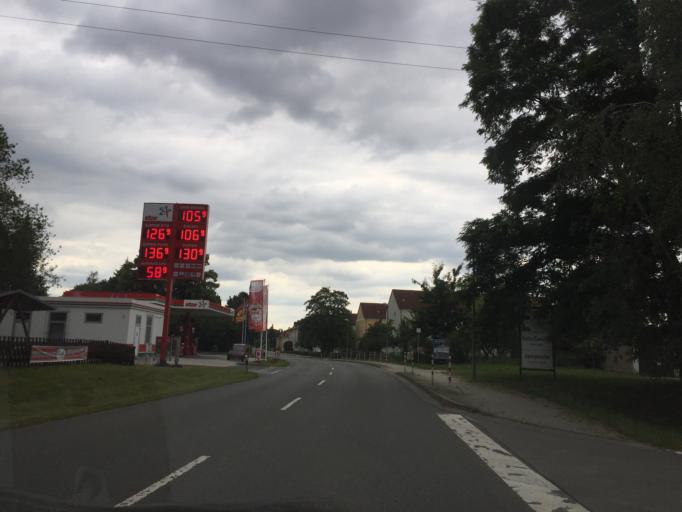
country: DE
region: Thuringia
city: Gossnitz
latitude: 50.8991
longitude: 12.4393
